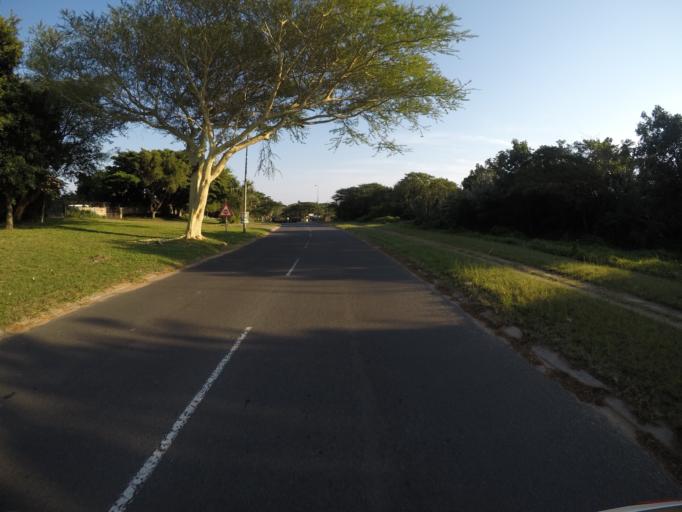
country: ZA
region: KwaZulu-Natal
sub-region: uThungulu District Municipality
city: Richards Bay
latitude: -28.7788
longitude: 32.1105
